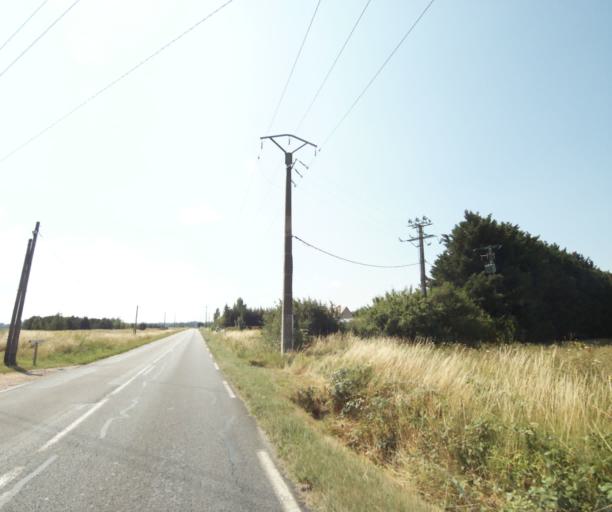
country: FR
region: Centre
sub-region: Departement du Loiret
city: Saint-Cyr-en-Val
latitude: 47.8442
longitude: 1.9587
